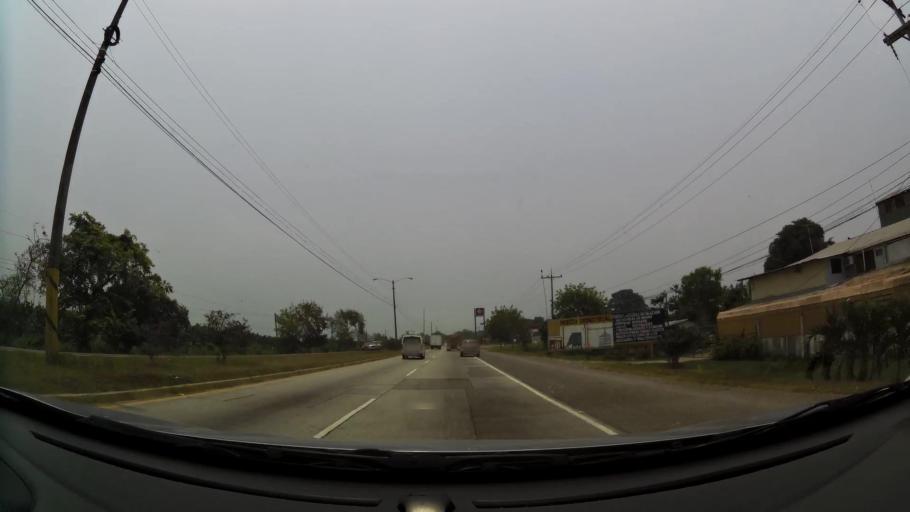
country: HN
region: Yoro
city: El Progreso
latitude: 15.4107
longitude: -87.8425
